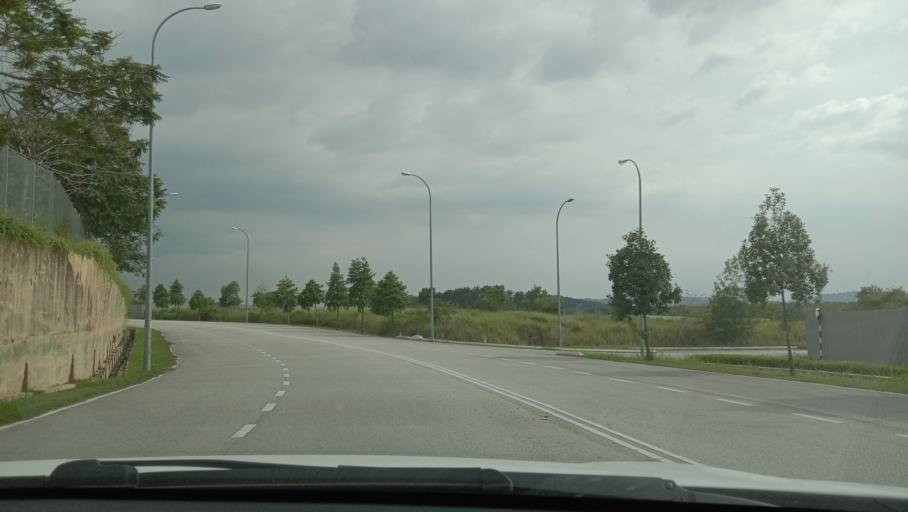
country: MY
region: Selangor
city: Ladang Seri Kundang
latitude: 3.2442
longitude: 101.4773
